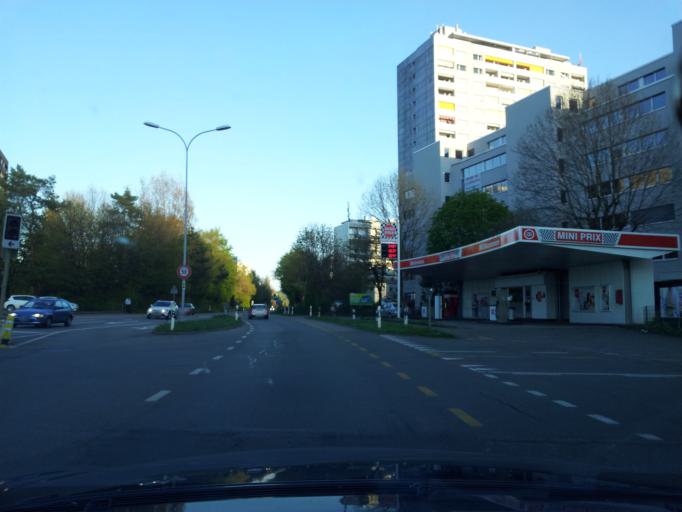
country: CH
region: Bern
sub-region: Biel/Bienne District
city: Nidau
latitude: 47.1271
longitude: 7.2446
